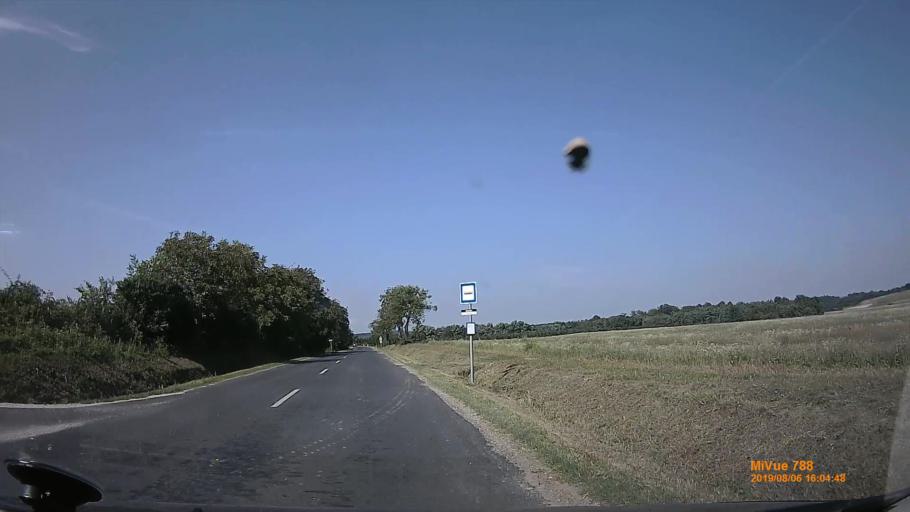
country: HU
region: Zala
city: Murakeresztur
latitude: 46.3068
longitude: 16.9599
